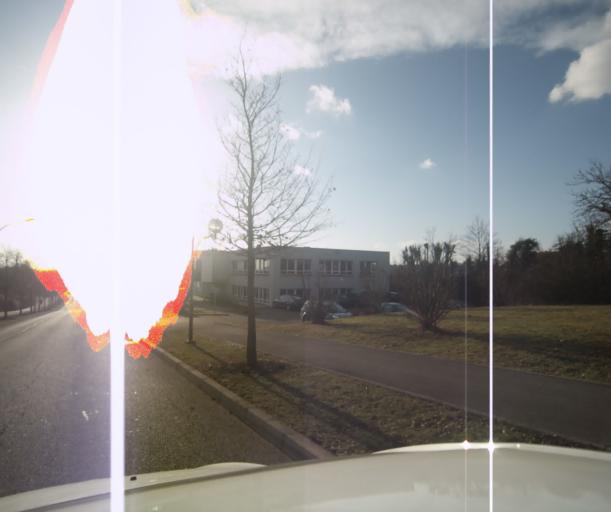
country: FR
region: Franche-Comte
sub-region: Departement du Doubs
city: Besancon
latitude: 47.2573
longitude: 6.0055
